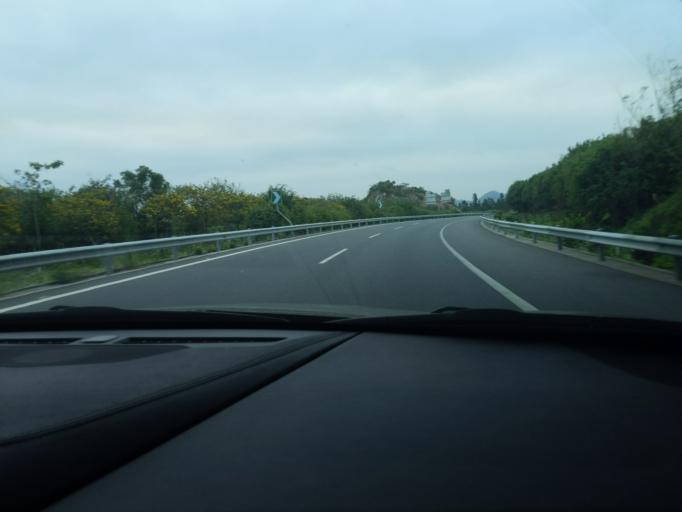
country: CN
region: Fujian
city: Neikeng
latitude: 24.7866
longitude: 118.4784
